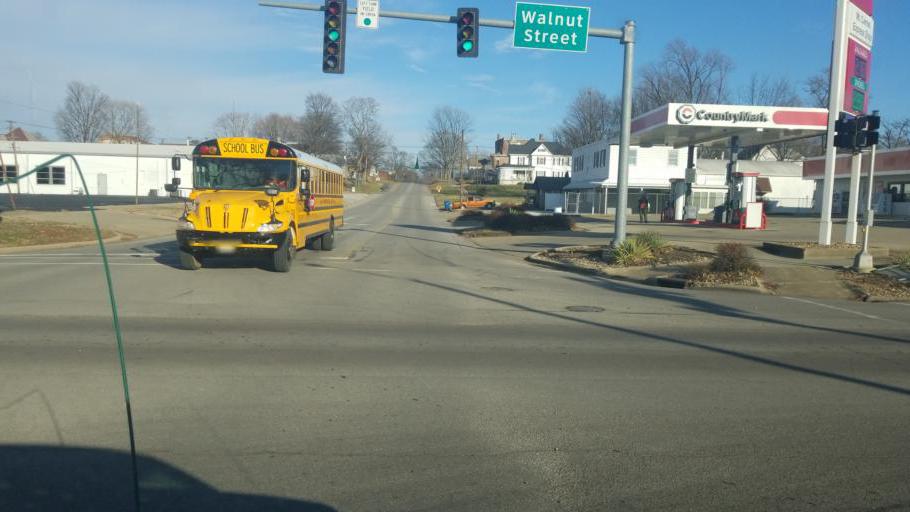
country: US
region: Illinois
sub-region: Wabash County
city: Mount Carmel
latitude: 38.4071
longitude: -87.7634
